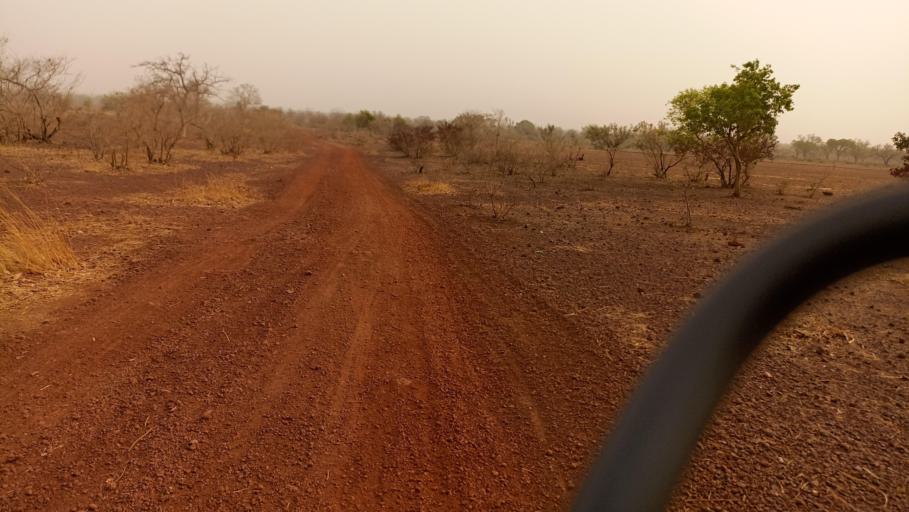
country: BF
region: Nord
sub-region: Province du Zondoma
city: Gourcy
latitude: 13.1516
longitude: -2.5956
